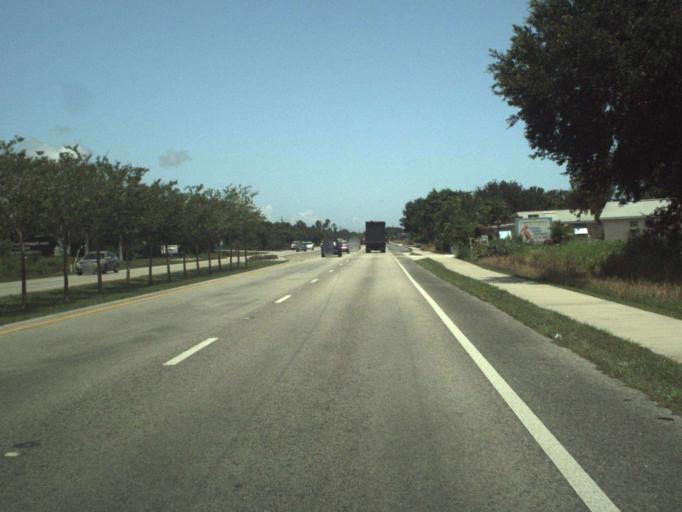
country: US
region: Florida
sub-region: Indian River County
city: Sebastian
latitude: 27.7992
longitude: -80.4611
